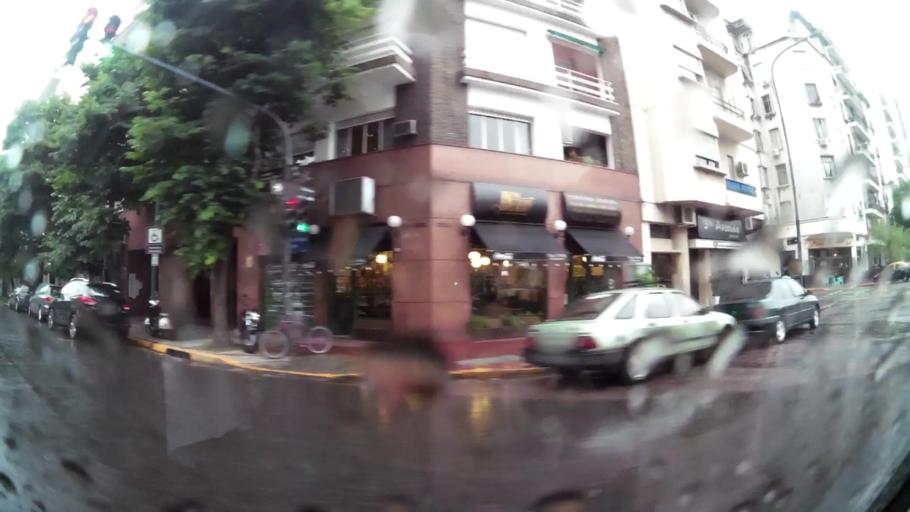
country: AR
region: Buenos Aires F.D.
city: Buenos Aires
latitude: -34.6294
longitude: -58.3707
